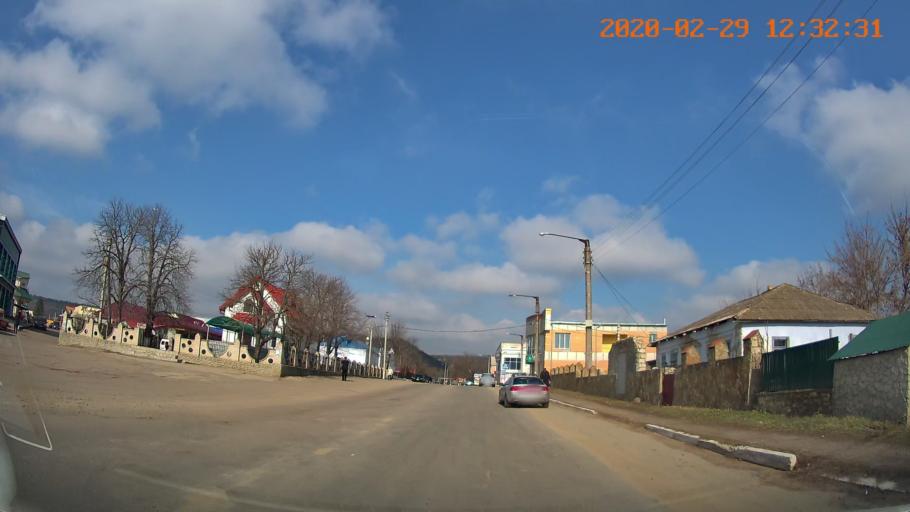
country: MD
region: Telenesti
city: Camenca
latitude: 48.0291
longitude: 28.7031
